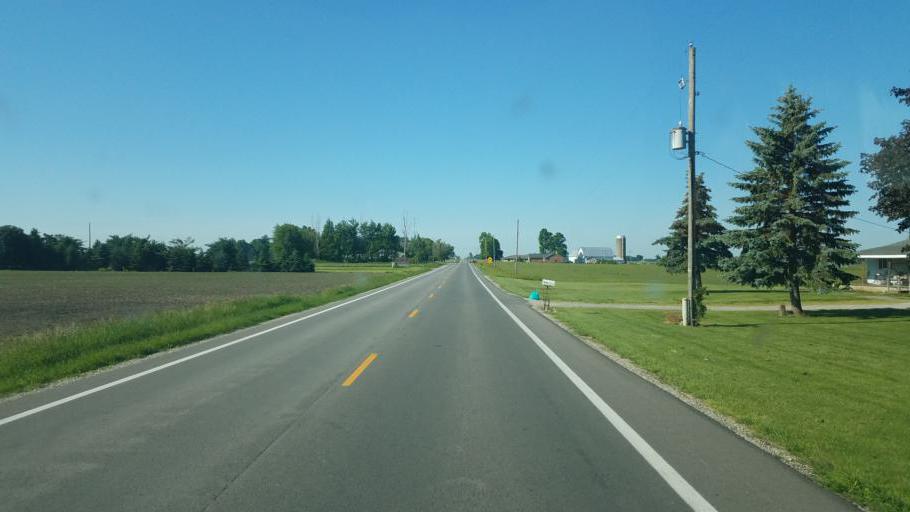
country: US
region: Ohio
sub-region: Crawford County
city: Bucyrus
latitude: 40.7793
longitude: -82.9818
